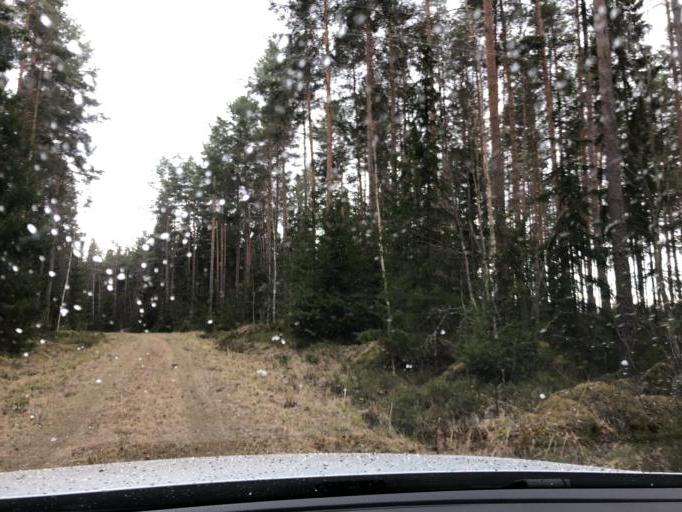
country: SE
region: Gaevleborg
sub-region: Gavle Kommun
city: Hedesunda
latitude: 60.3417
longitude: 17.0820
